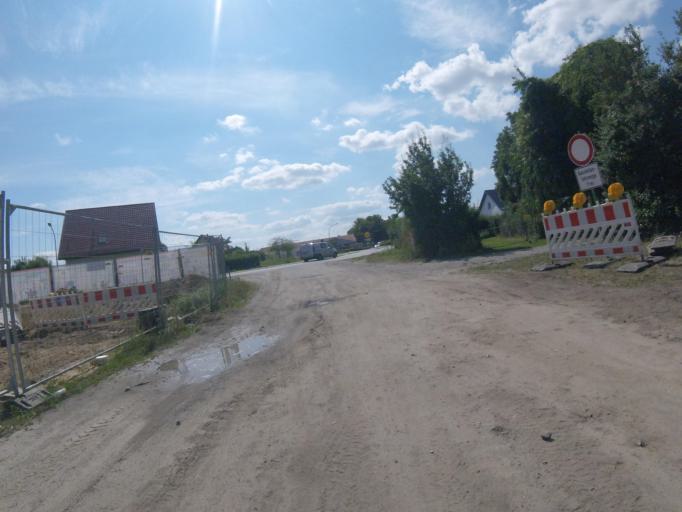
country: DE
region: Brandenburg
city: Wildau
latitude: 52.3243
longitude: 13.6162
